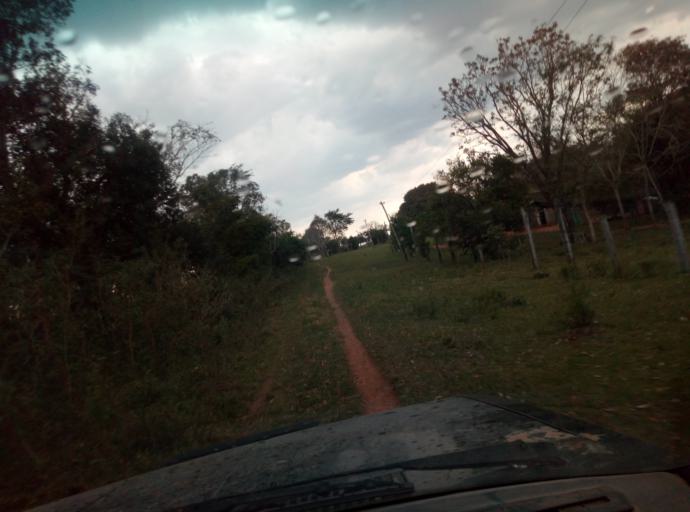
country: PY
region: Caaguazu
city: Doctor Cecilio Baez
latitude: -25.1475
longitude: -56.2212
